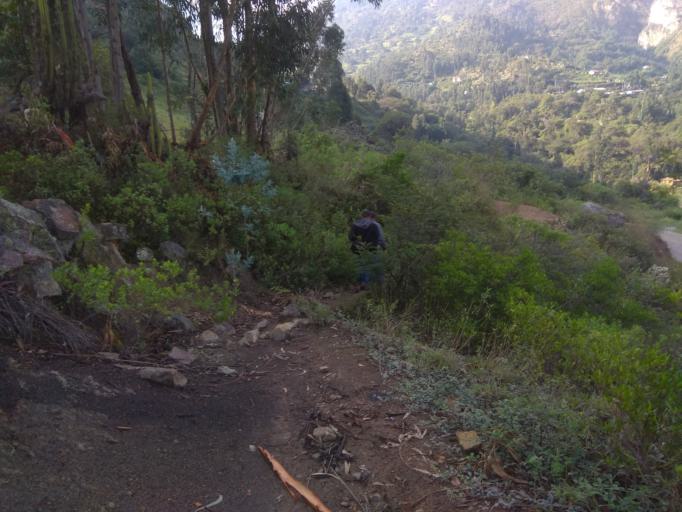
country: CO
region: Boyaca
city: Socha Viejo
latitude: 5.9847
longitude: -72.7027
